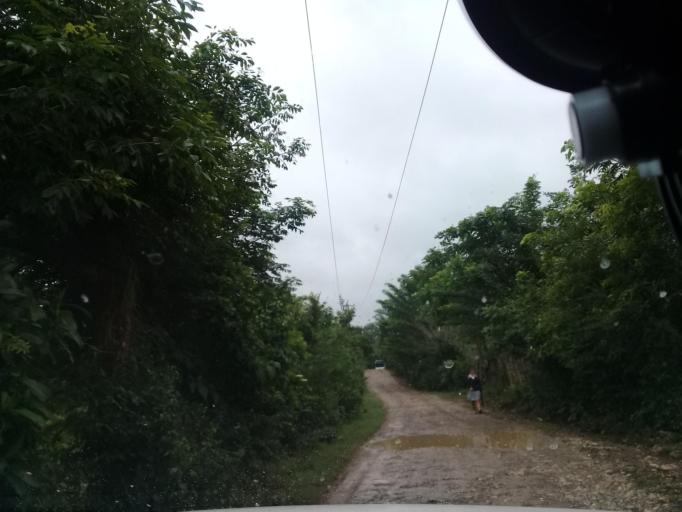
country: MX
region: Veracruz
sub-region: Chalma
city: San Pedro Coyutla
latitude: 21.2348
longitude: -98.4191
